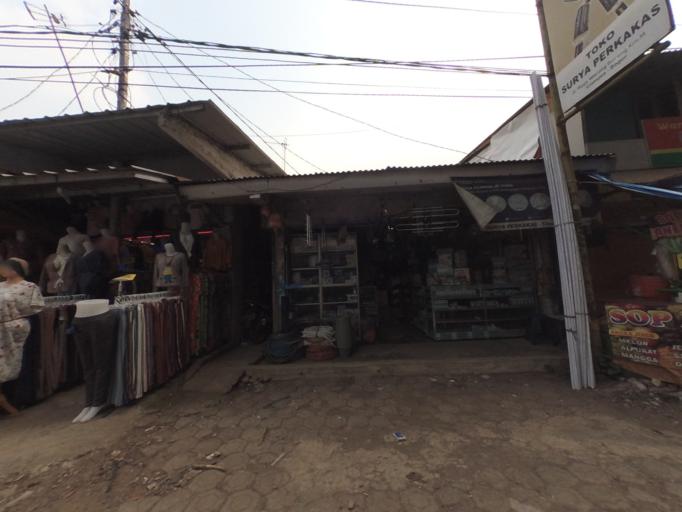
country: ID
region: West Java
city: Ciampea
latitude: -6.5565
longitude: 106.6950
